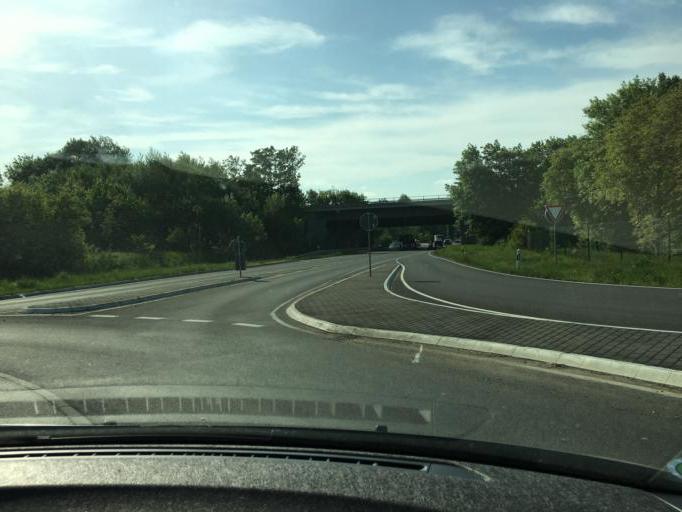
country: DE
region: North Rhine-Westphalia
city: Bruhl
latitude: 50.8033
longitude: 6.9070
